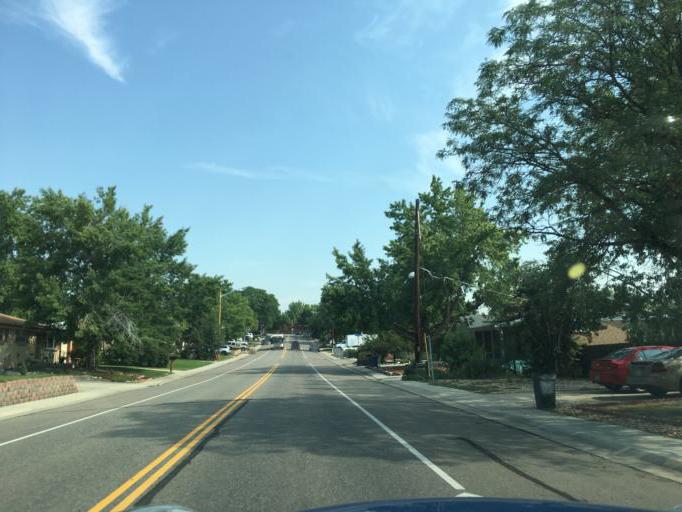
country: US
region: Colorado
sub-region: Jefferson County
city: Arvada
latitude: 39.8250
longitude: -105.0674
